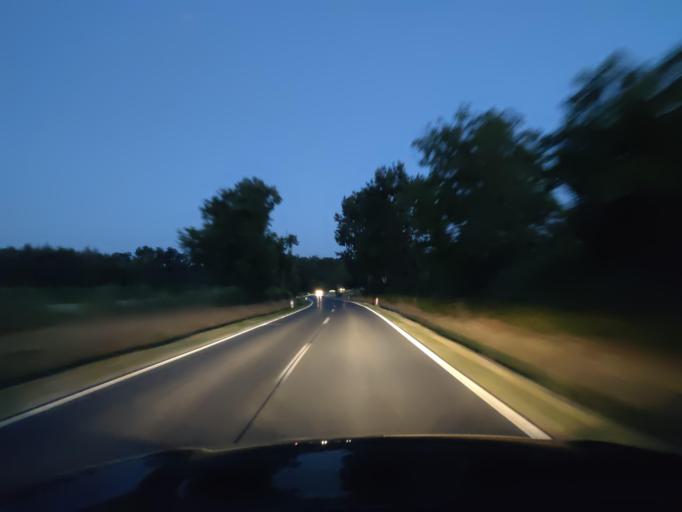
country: HR
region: Medimurska
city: Vratisinec
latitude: 46.4603
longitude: 16.4292
